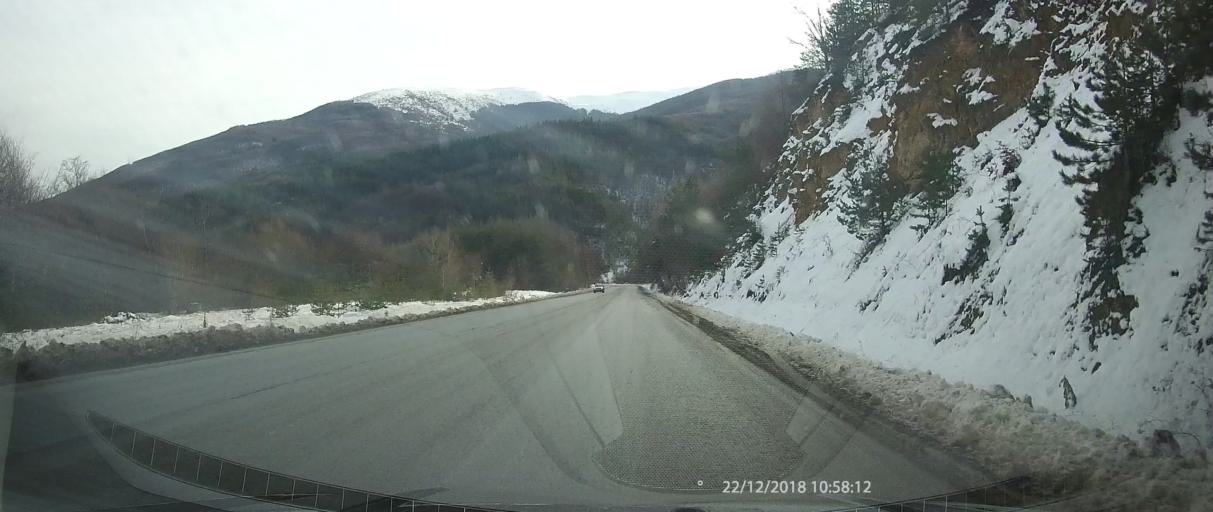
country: MK
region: Kriva Palanka
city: Kriva Palanka
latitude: 42.2185
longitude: 22.4667
